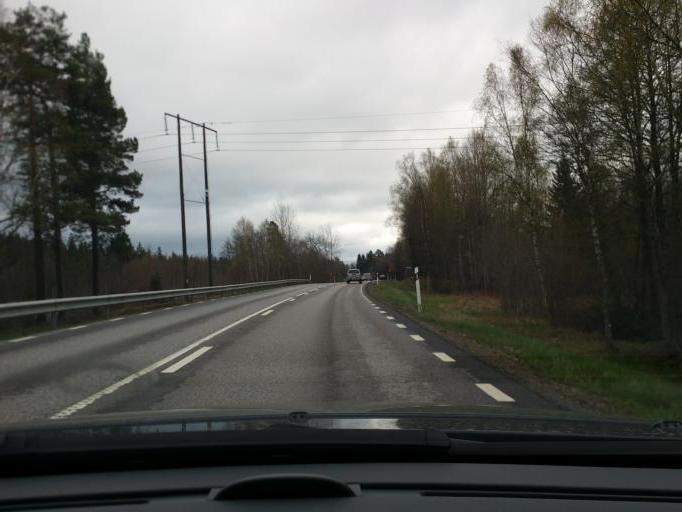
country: SE
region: Kronoberg
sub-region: Vaxjo Kommun
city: Vaexjoe
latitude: 56.8344
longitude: 14.8646
